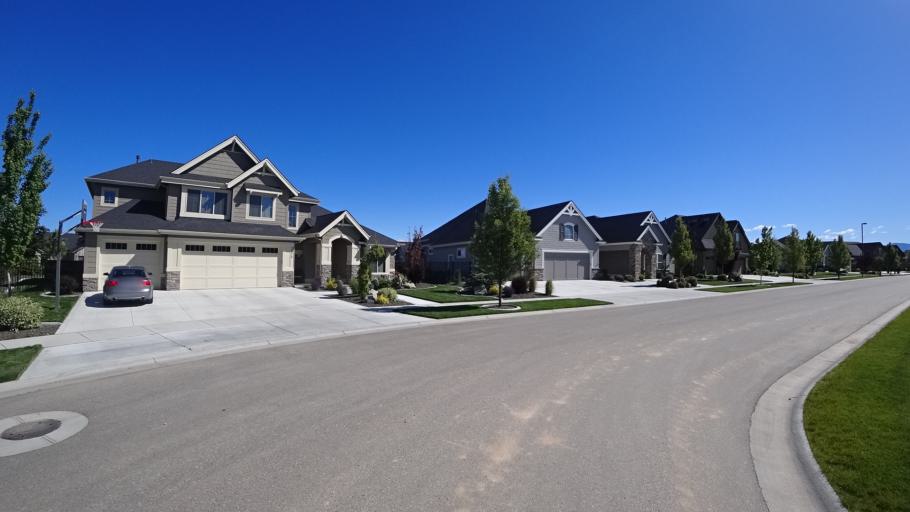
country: US
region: Idaho
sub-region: Ada County
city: Eagle
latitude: 43.6669
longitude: -116.3994
